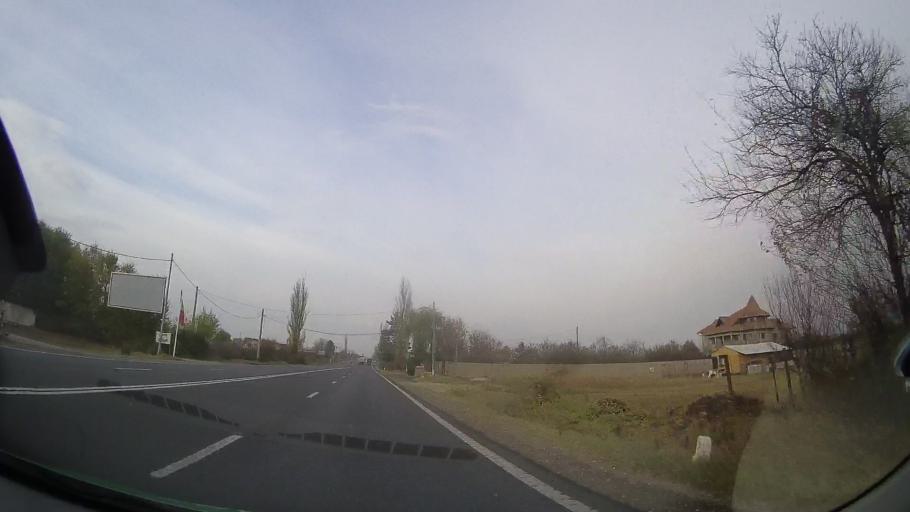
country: RO
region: Prahova
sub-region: Comuna Gorgota
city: Potigrafu
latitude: 44.7706
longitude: 26.1022
